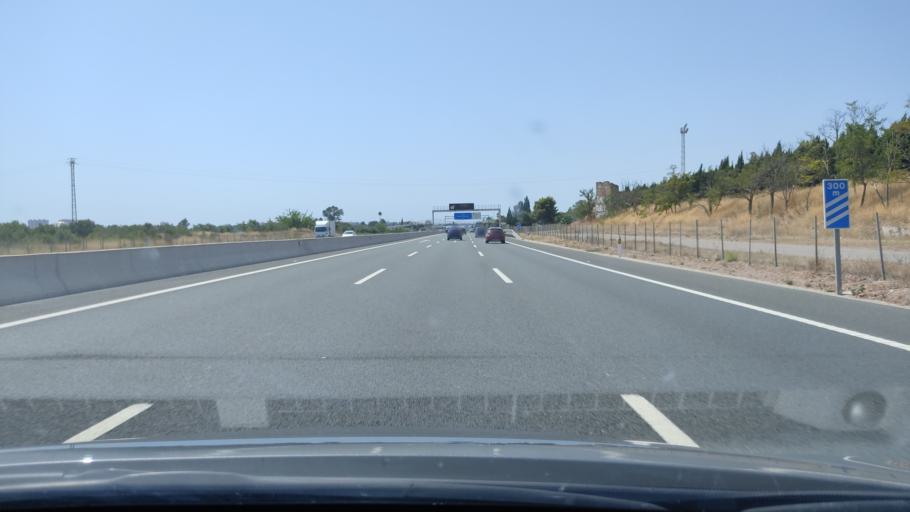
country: ES
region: Valencia
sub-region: Provincia de Valencia
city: Puig
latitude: 39.5929
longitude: -0.2932
